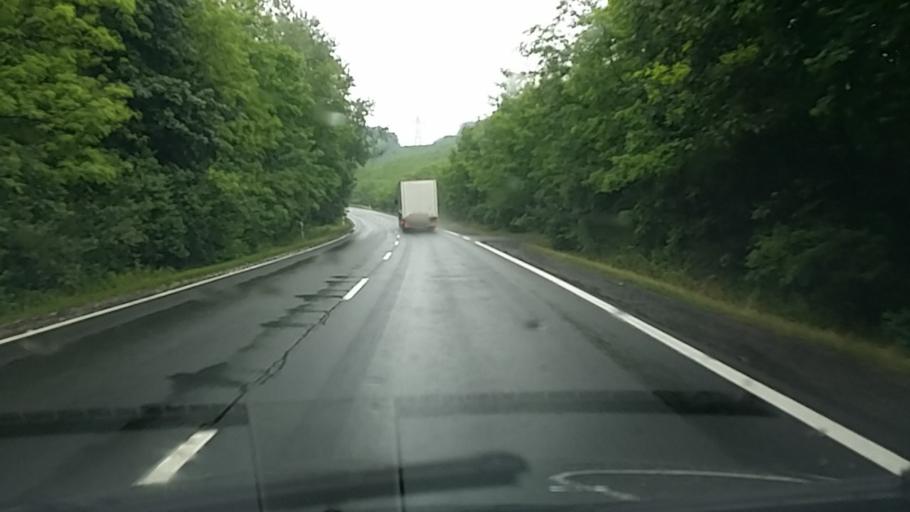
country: HU
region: Nograd
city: Retsag
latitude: 47.9540
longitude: 19.1439
